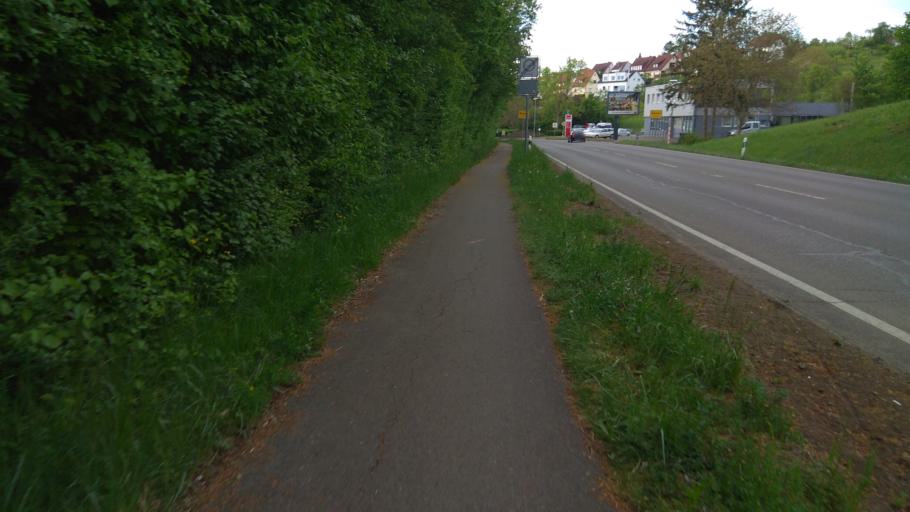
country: DE
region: Baden-Wuerttemberg
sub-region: Tuebingen Region
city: Wannweil
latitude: 48.5070
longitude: 9.1633
